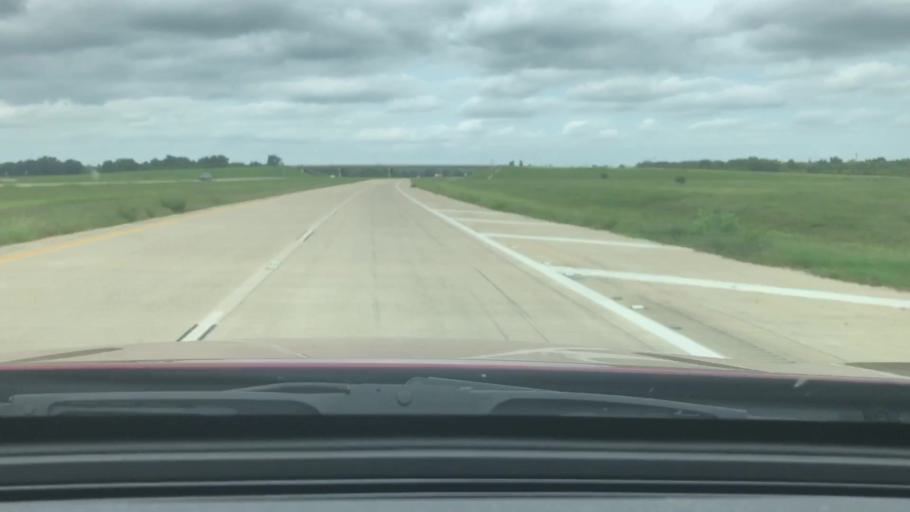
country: US
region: Louisiana
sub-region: Caddo Parish
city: Oil City
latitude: 32.7636
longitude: -93.8871
